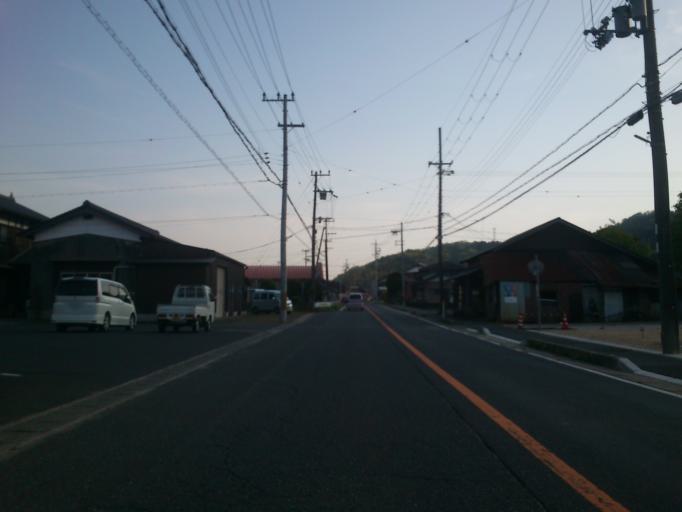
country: JP
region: Kyoto
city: Miyazu
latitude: 35.5581
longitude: 135.1400
